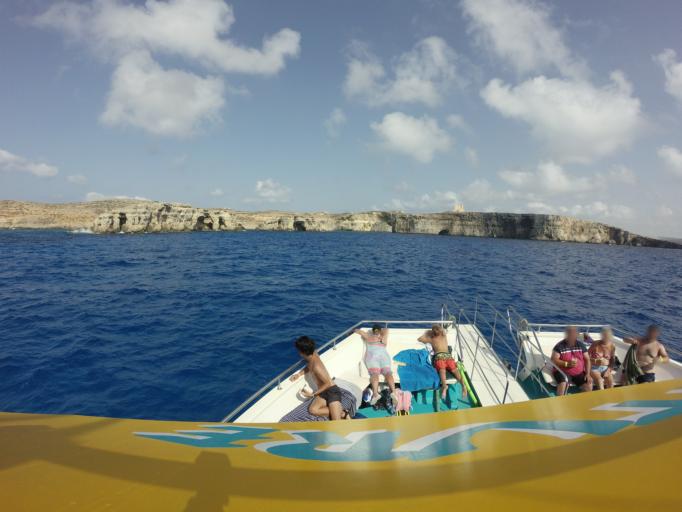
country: MT
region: Il-Qala
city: Qala
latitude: 36.0099
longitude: 14.3223
